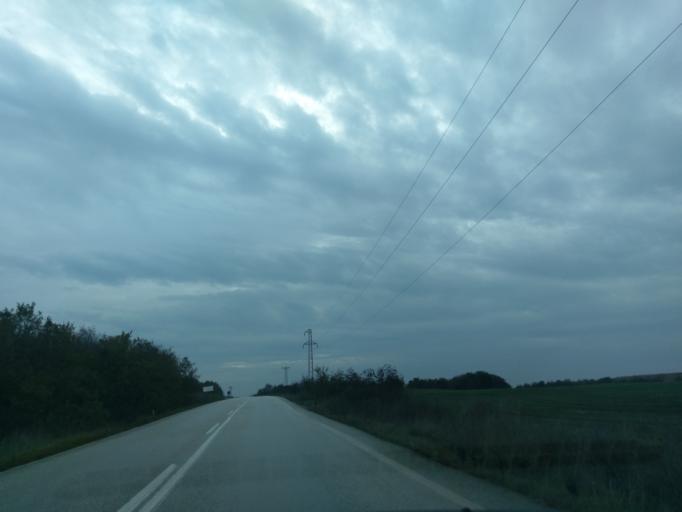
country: TR
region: Istanbul
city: Canta
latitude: 41.1756
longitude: 28.0905
